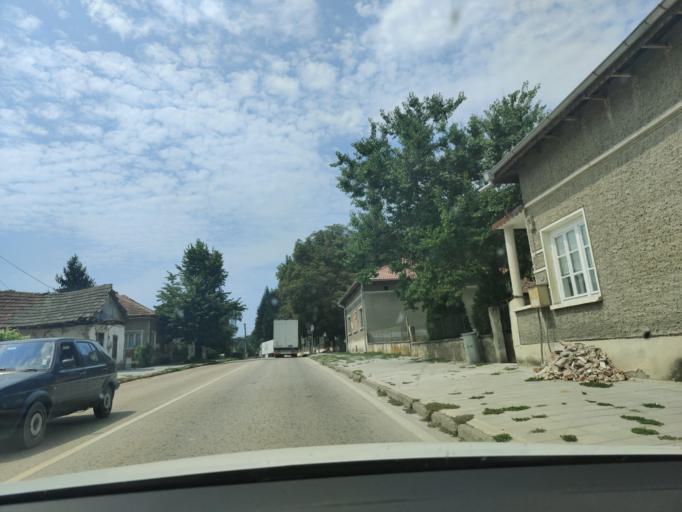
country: BG
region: Vidin
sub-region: Obshtina Dimovo
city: Dimovo
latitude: 43.7466
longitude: 22.7322
